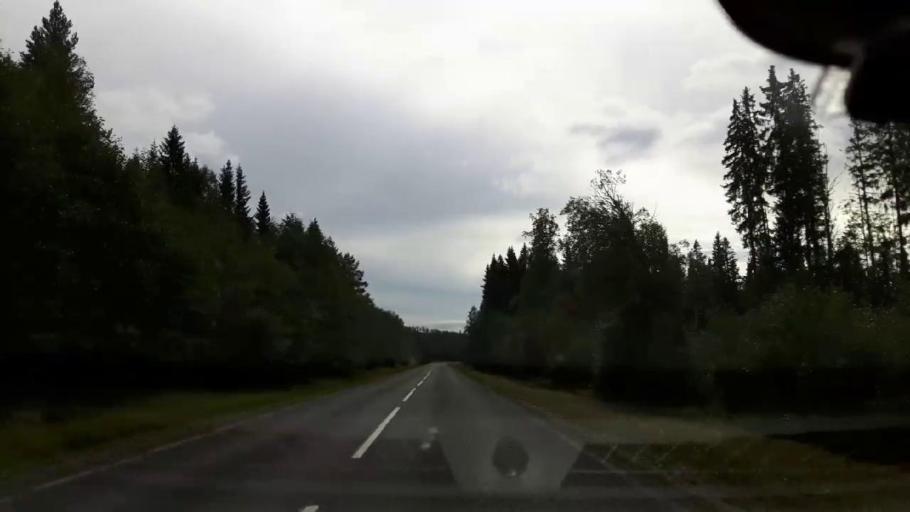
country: SE
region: Jaemtland
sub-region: Ragunda Kommun
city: Hammarstrand
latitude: 63.0937
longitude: 15.9176
